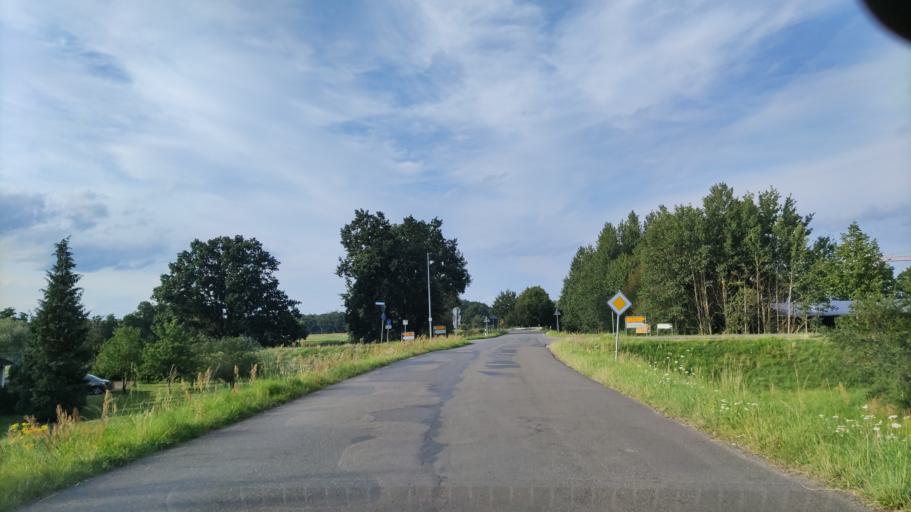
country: DE
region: Lower Saxony
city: Dannenberg
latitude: 53.1063
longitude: 11.1096
